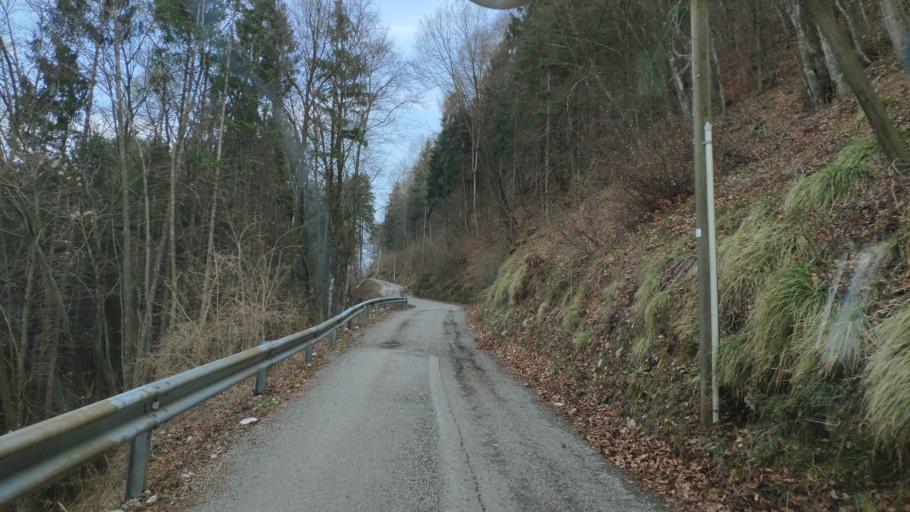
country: IT
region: Veneto
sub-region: Provincia di Vicenza
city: Enego
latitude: 45.9510
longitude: 11.7076
